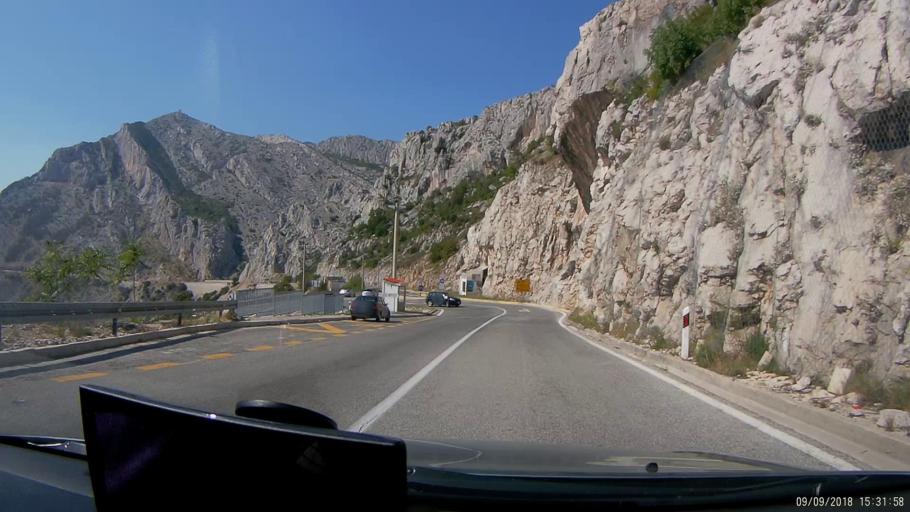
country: HR
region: Splitsko-Dalmatinska
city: Donja Brela
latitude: 43.4015
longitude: 16.8929
